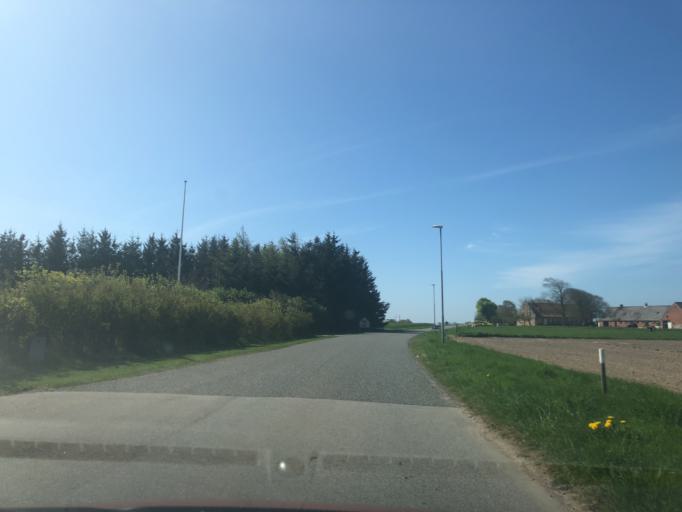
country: DK
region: Central Jutland
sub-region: Holstebro Kommune
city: Vinderup
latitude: 56.5883
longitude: 8.7792
